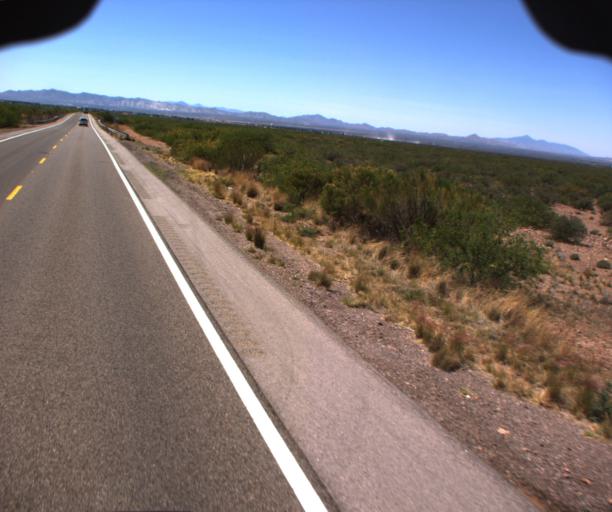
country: US
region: Arizona
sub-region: Cochise County
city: Douglas
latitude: 31.4034
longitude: -109.5026
